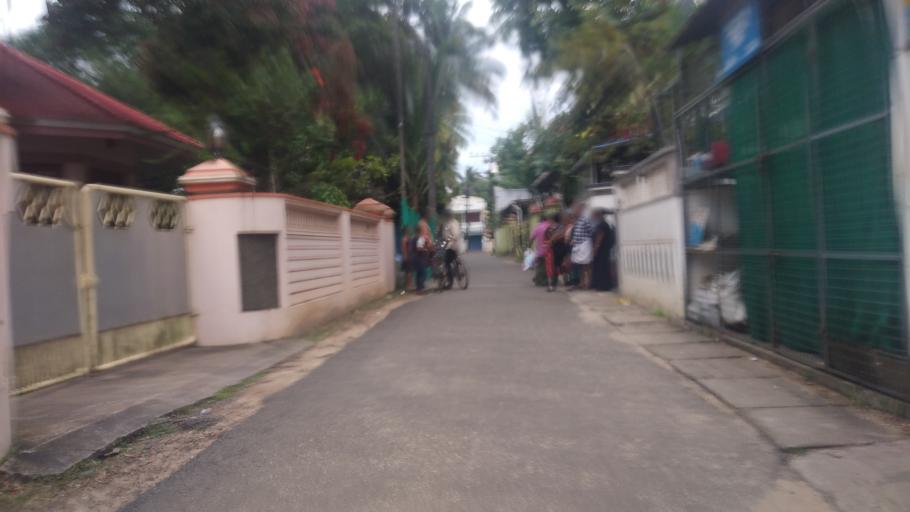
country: IN
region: Kerala
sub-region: Alappuzha
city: Arukutti
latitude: 9.8732
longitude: 76.2885
